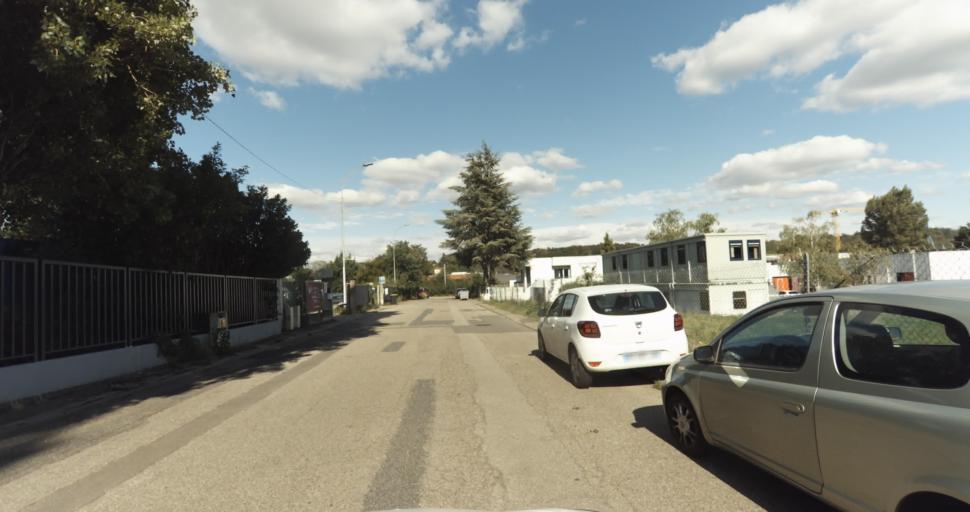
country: FR
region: Rhone-Alpes
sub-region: Departement du Rhone
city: Chaponost
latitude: 45.6965
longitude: 4.7618
